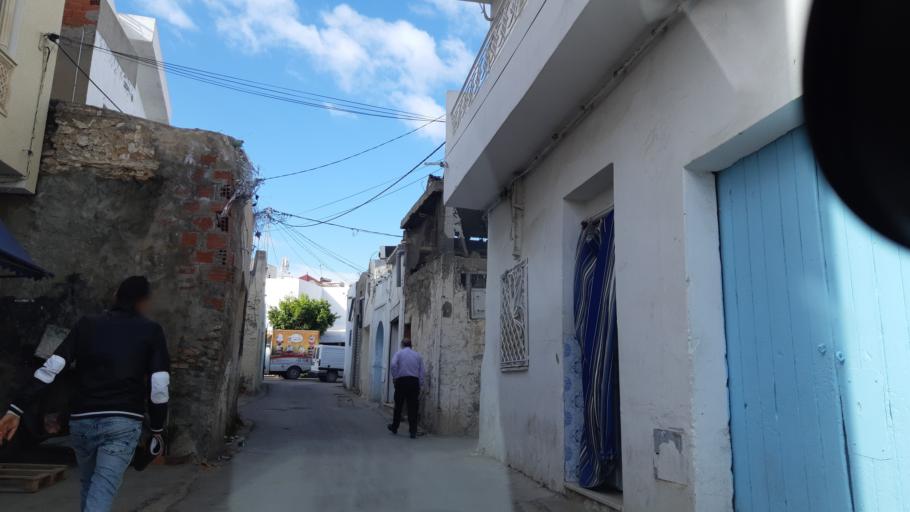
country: TN
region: Susah
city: Akouda
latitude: 35.8725
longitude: 10.5364
